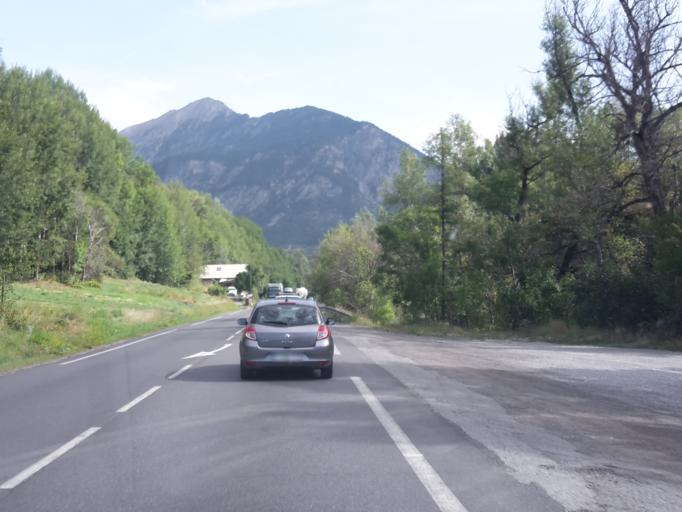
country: FR
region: Provence-Alpes-Cote d'Azur
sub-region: Departement des Hautes-Alpes
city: Villar-Saint-Pancrace
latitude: 44.8831
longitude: 6.6221
